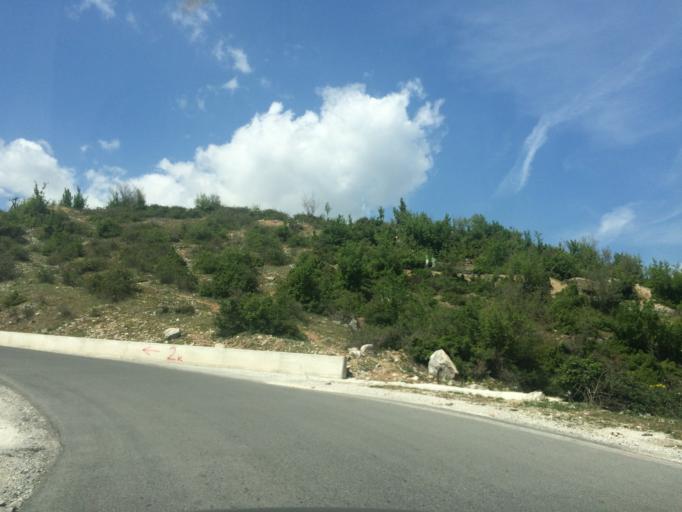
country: AL
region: Kukes
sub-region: Rrethi i Tropojes
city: Bajram Curri
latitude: 42.3581
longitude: 20.0959
